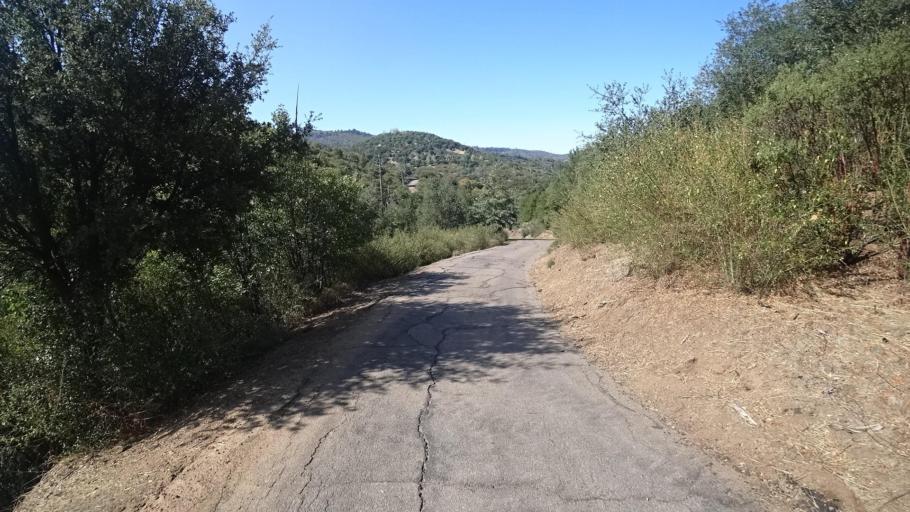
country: US
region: California
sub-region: San Diego County
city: Julian
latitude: 33.0254
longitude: -116.5675
